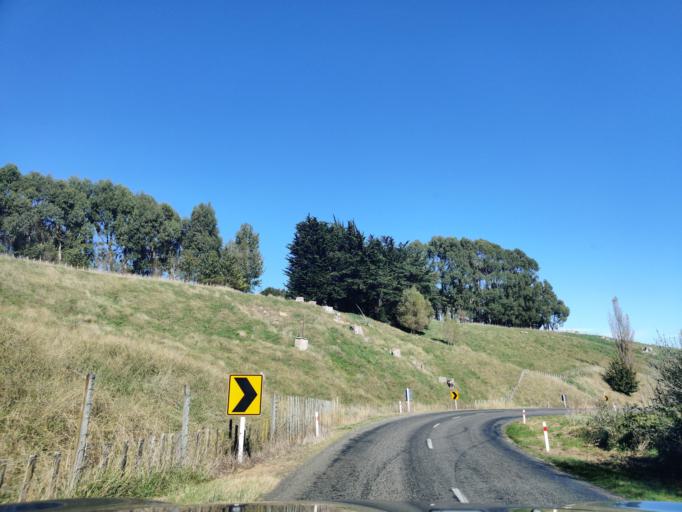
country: NZ
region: Manawatu-Wanganui
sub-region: Palmerston North City
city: Palmerston North
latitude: -40.2591
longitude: 175.7144
